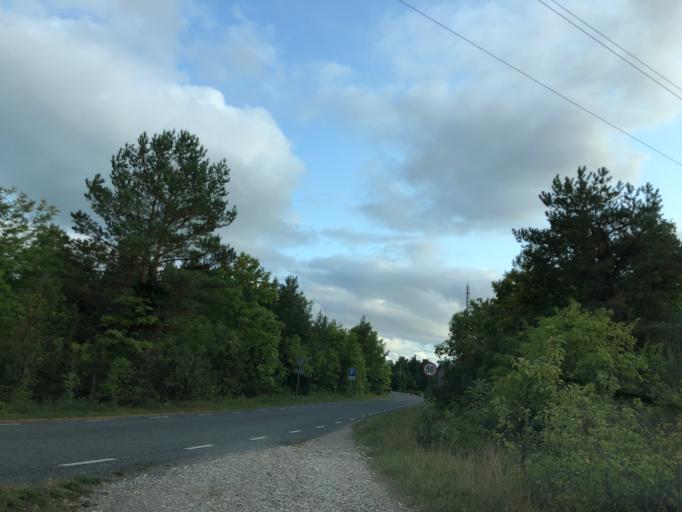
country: EE
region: Hiiumaa
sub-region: Kaerdla linn
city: Kardla
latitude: 58.7888
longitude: 22.8320
